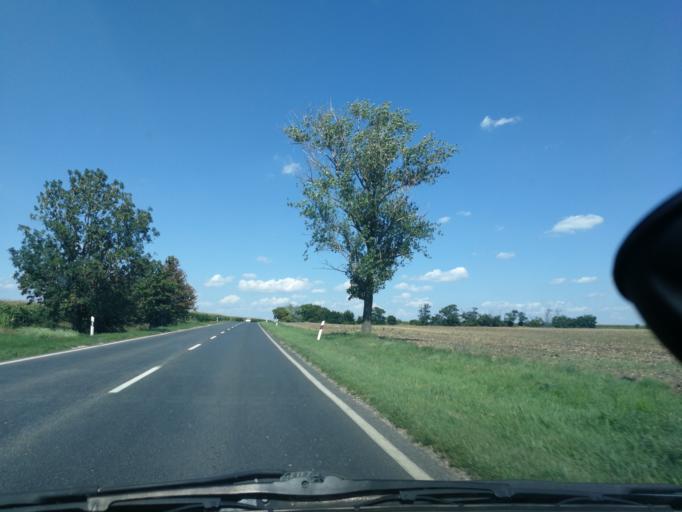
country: HU
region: Fejer
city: Martonvasar
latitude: 47.3273
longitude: 18.8041
